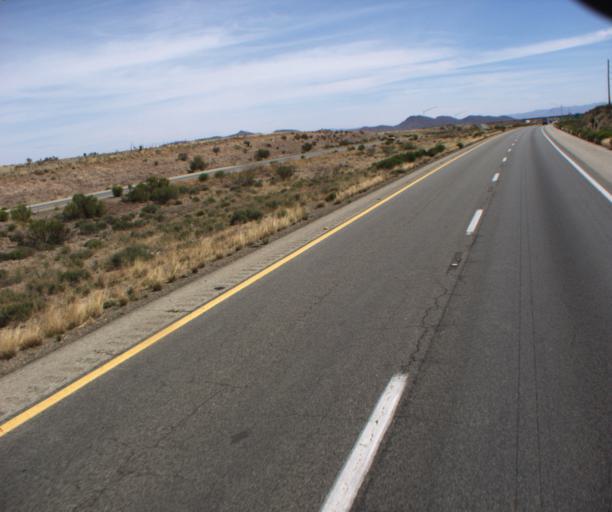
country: US
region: Arizona
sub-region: Cochise County
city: Willcox
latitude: 32.3574
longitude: -109.6919
